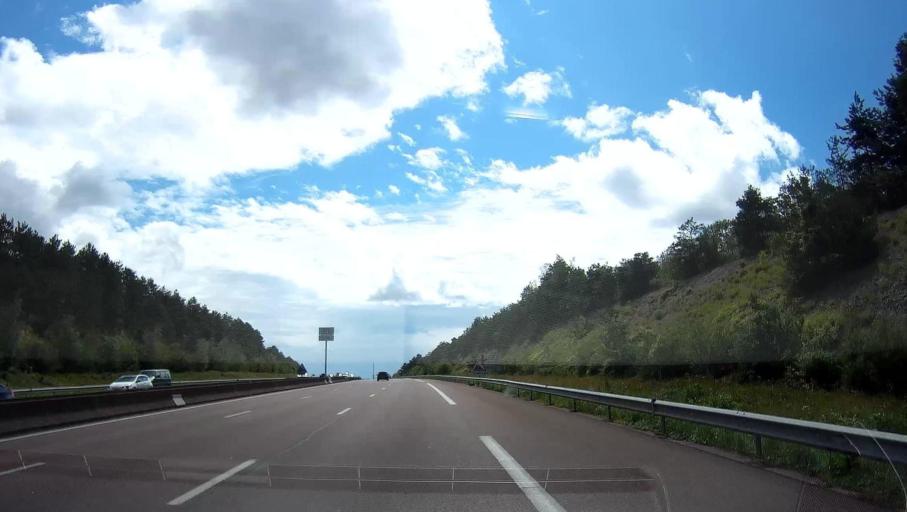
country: FR
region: Bourgogne
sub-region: Departement de la Cote-d'Or
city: Selongey
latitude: 47.5623
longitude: 5.1999
